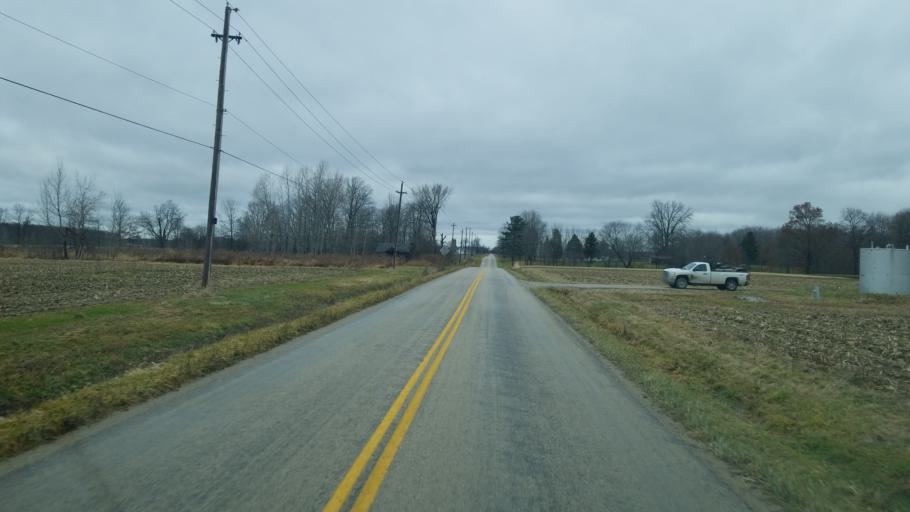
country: US
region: Ohio
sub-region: Ashtabula County
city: Jefferson
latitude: 41.7531
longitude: -80.6226
